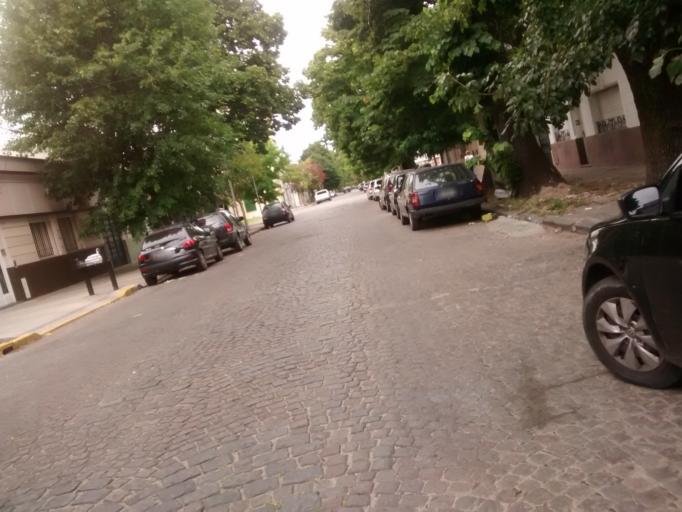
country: AR
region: Buenos Aires
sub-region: Partido de La Plata
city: La Plata
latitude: -34.9237
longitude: -57.9334
